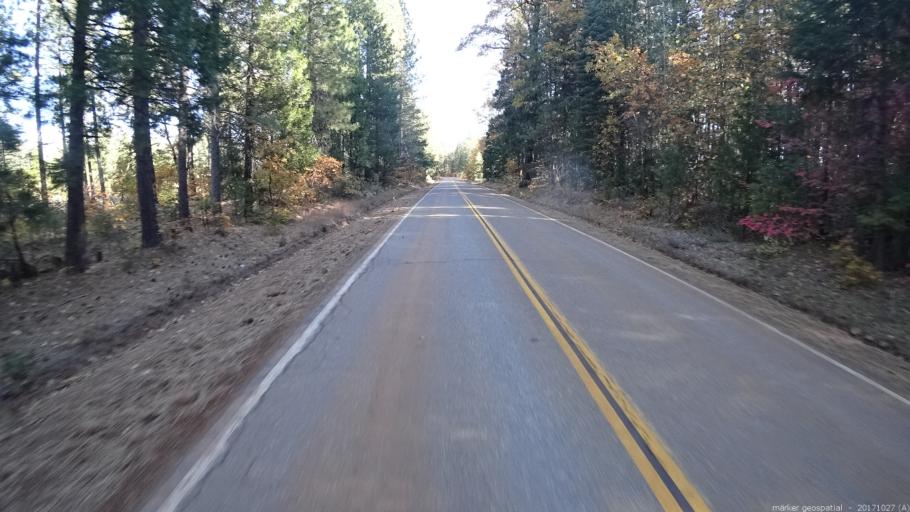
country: US
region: California
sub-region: Shasta County
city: Burney
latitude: 40.9583
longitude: -121.9428
